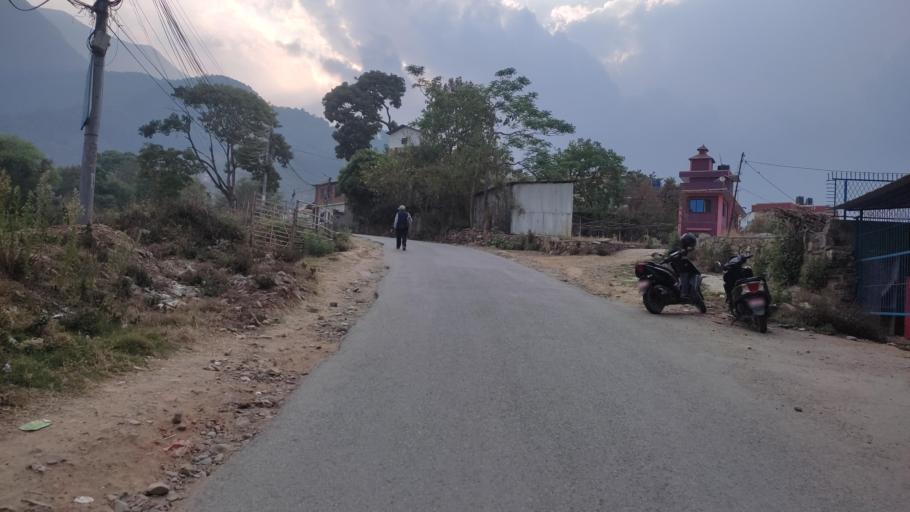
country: NP
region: Central Region
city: Kirtipur
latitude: 27.6666
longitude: 85.2580
